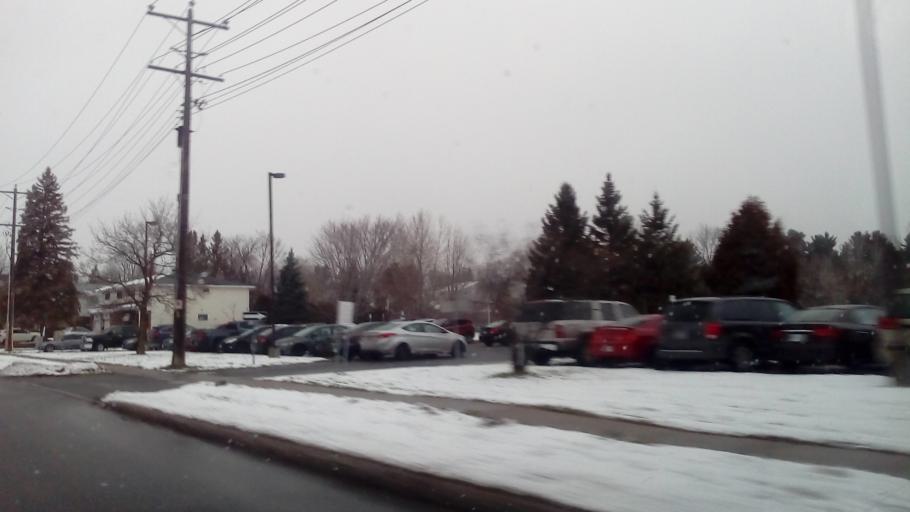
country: CA
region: Ontario
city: Ottawa
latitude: 45.4330
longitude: -75.5653
